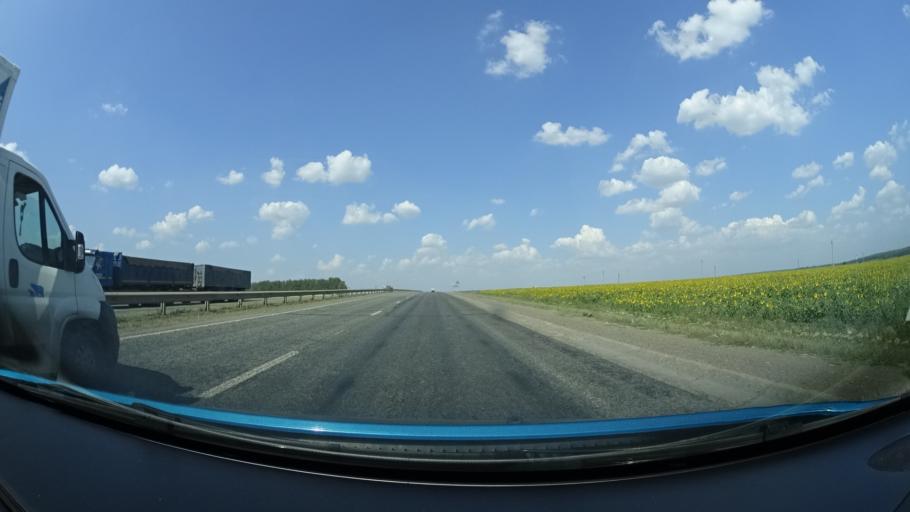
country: RU
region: Bashkortostan
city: Dmitriyevka
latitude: 54.6822
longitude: 55.3283
